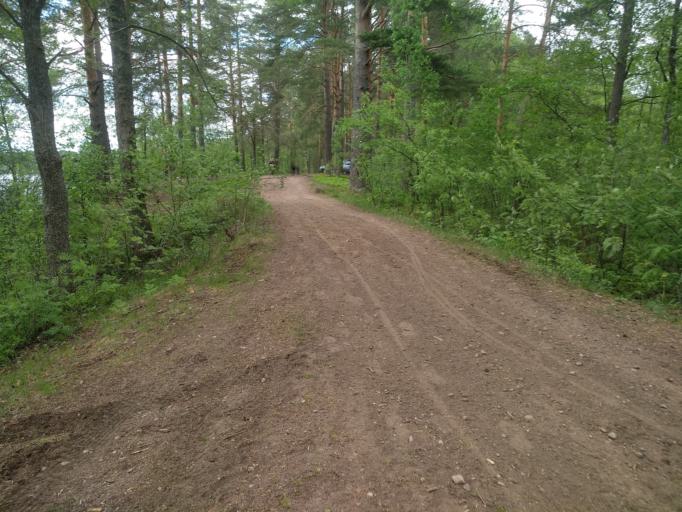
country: RU
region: Leningrad
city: Michurinskoye
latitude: 60.5980
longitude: 29.8769
